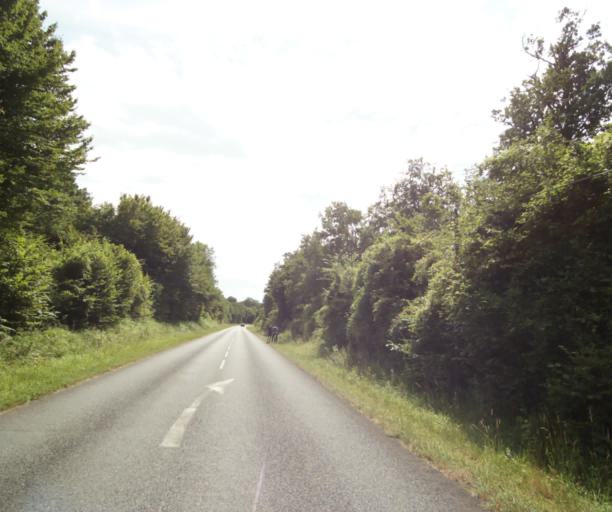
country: FR
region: Ile-de-France
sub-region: Departement de Seine-et-Marne
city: Dammarie-les-Lys
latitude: 48.4935
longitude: 2.6320
